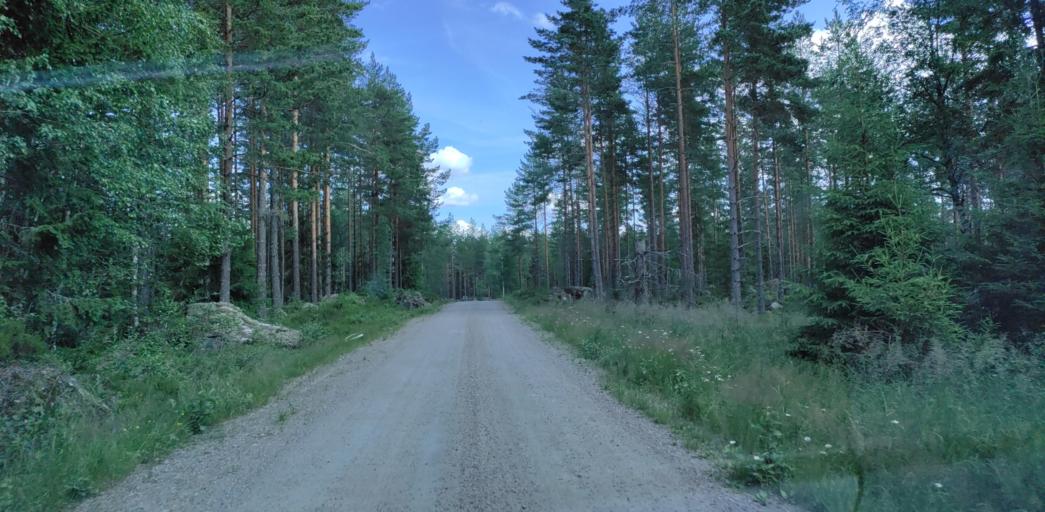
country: SE
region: Vaermland
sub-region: Hagfors Kommun
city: Ekshaerad
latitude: 60.0957
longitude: 13.4207
